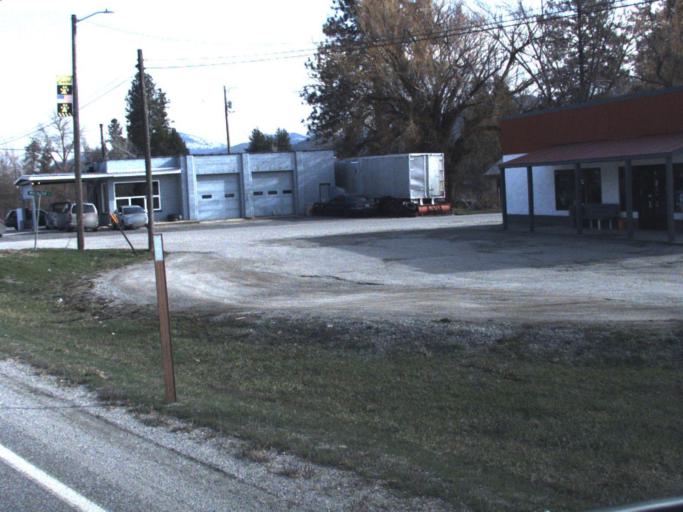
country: US
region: Washington
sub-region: Pend Oreille County
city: Newport
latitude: 48.3371
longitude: -117.3044
